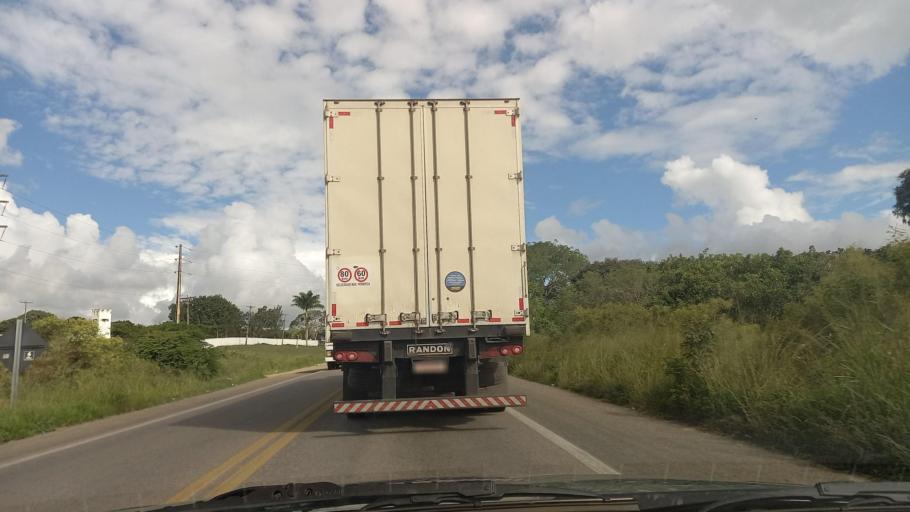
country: BR
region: Pernambuco
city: Garanhuns
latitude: -8.8654
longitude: -36.4625
